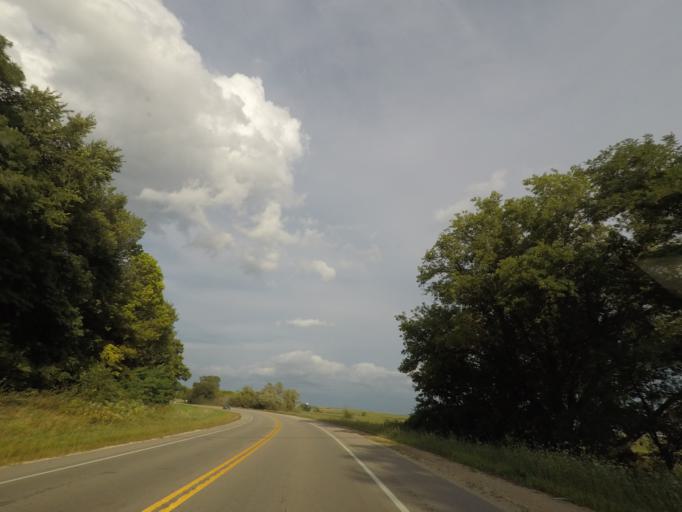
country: US
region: Wisconsin
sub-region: Dane County
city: Waunakee
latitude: 43.1879
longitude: -89.5040
